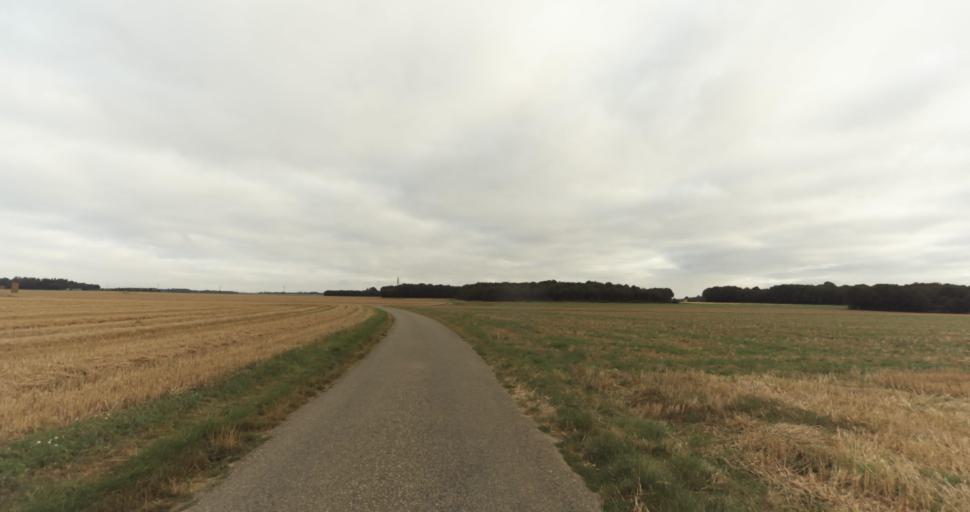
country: FR
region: Haute-Normandie
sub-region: Departement de l'Eure
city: Saint-Germain-sur-Avre
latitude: 48.7899
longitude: 1.2606
